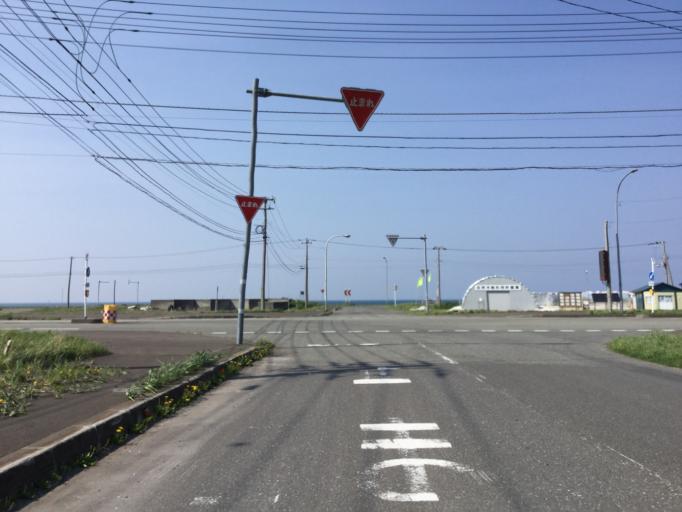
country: JP
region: Hokkaido
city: Makubetsu
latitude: 45.4028
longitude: 141.7669
